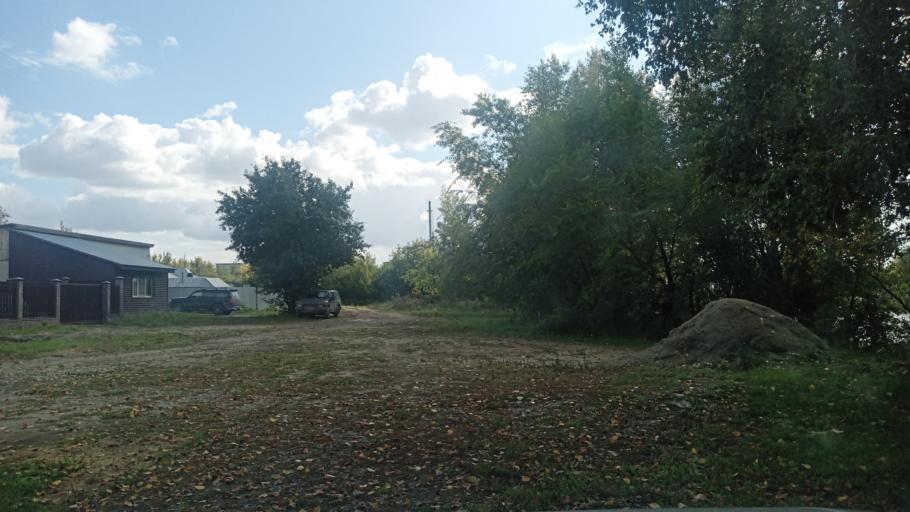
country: RU
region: Altai Krai
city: Zaton
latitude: 53.2989
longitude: 83.7997
